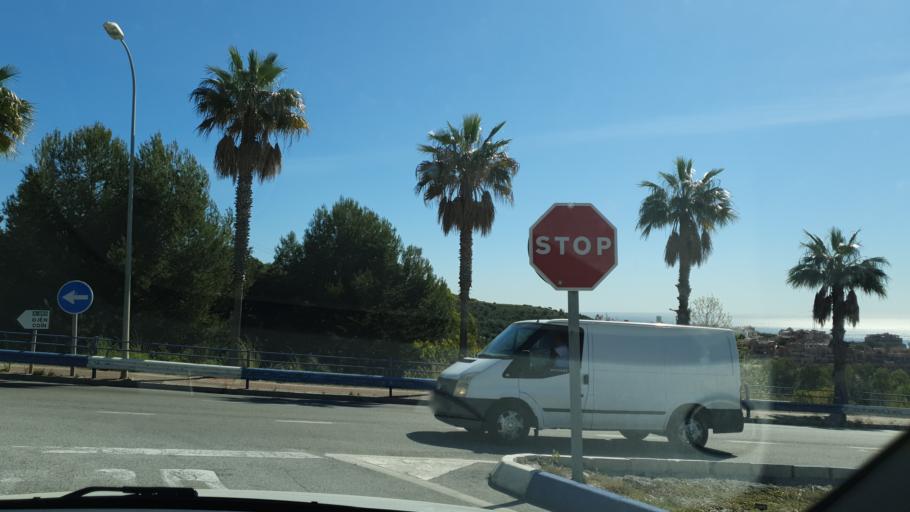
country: ES
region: Andalusia
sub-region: Provincia de Malaga
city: Marbella
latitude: 36.5277
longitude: -4.8819
